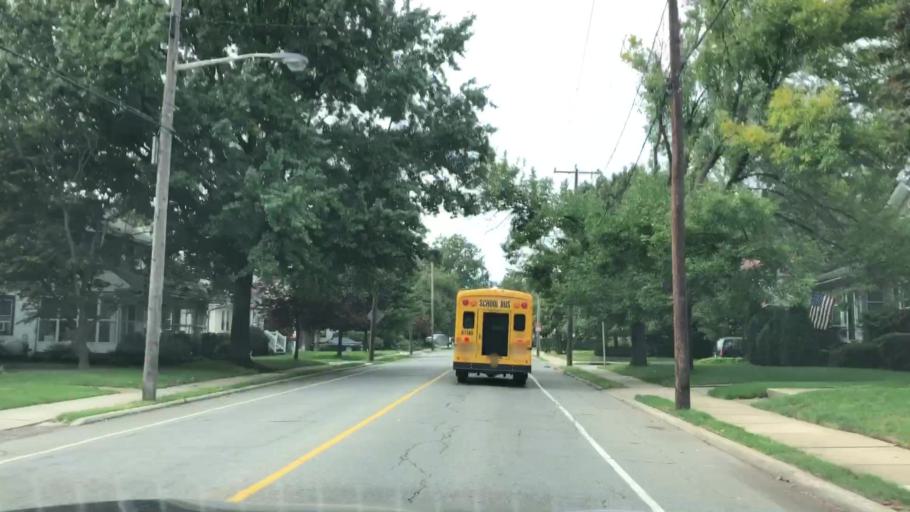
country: US
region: New York
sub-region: Nassau County
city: Floral Park
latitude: 40.7224
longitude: -73.6987
